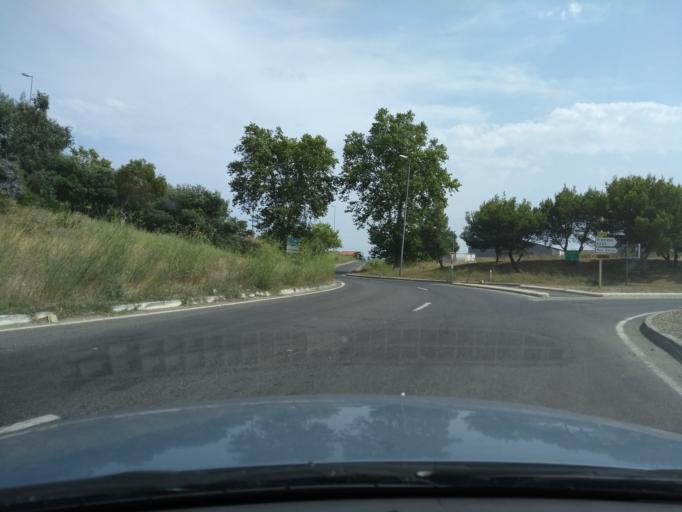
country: FR
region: Languedoc-Roussillon
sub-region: Departement des Pyrenees-Orientales
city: Saint-Esteve
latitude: 42.6942
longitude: 2.8501
